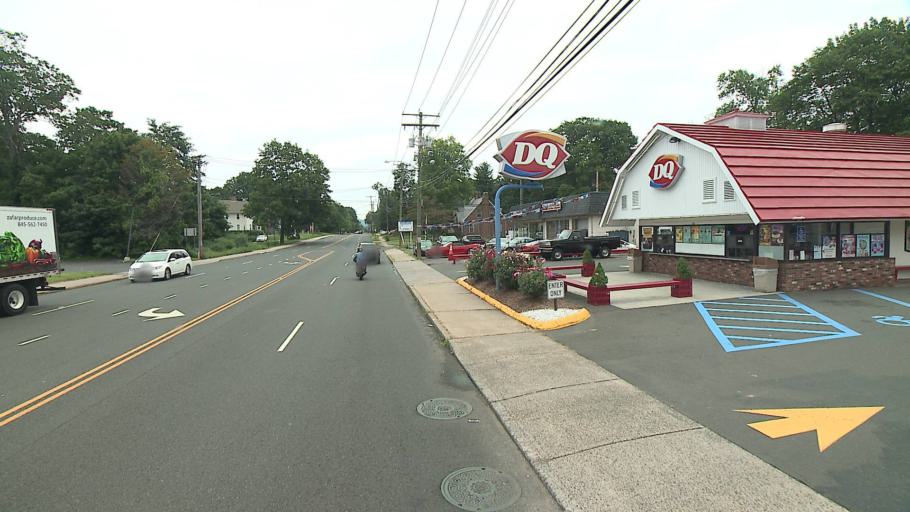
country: US
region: Connecticut
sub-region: New Haven County
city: Hamden
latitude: 41.3714
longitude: -72.9061
